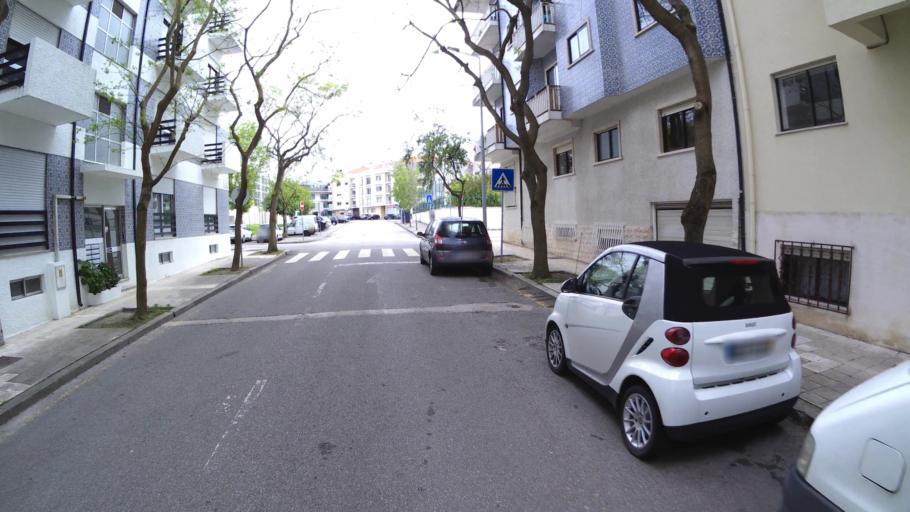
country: PT
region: Aveiro
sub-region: Aveiro
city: Aveiro
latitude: 40.6460
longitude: -8.6508
